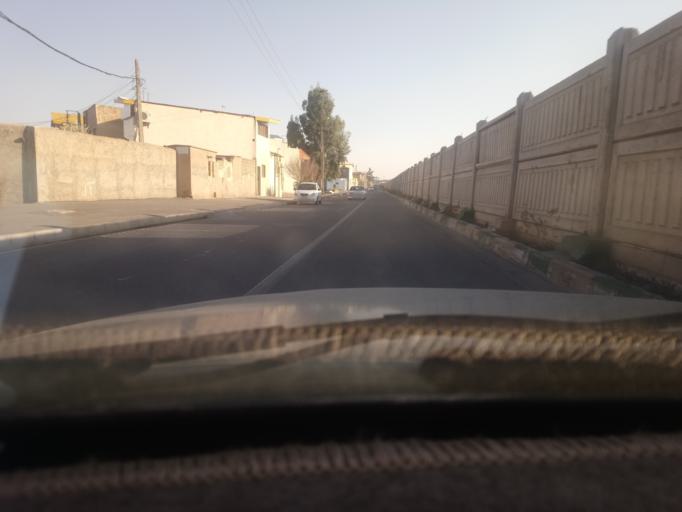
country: IR
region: Qom
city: Qom
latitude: 34.6653
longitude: 50.8673
